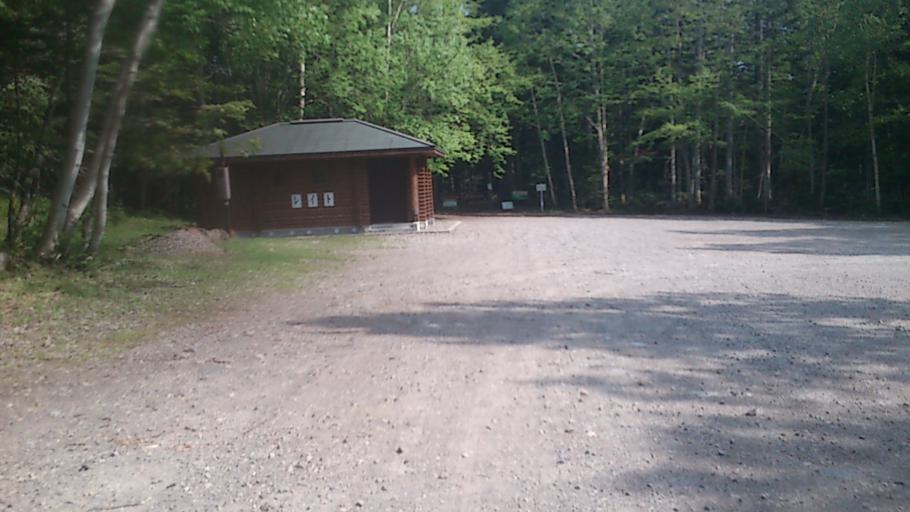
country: JP
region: Hokkaido
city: Kitami
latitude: 43.3799
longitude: 143.9709
